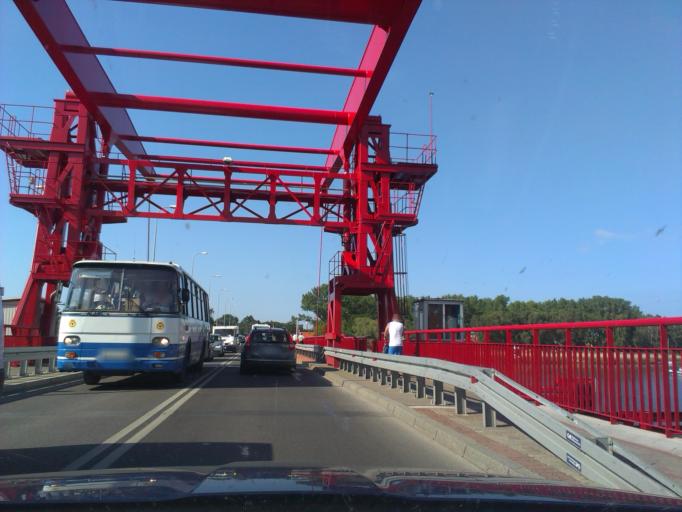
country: PL
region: West Pomeranian Voivodeship
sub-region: Powiat kamienski
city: Dziwnow
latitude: 54.0192
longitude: 14.7425
